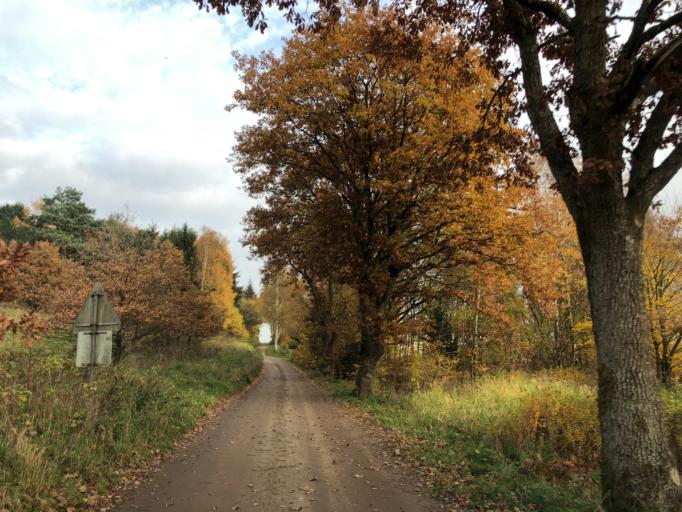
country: DK
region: Central Jutland
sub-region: Silkeborg Kommune
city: Silkeborg
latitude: 56.1456
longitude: 9.4864
